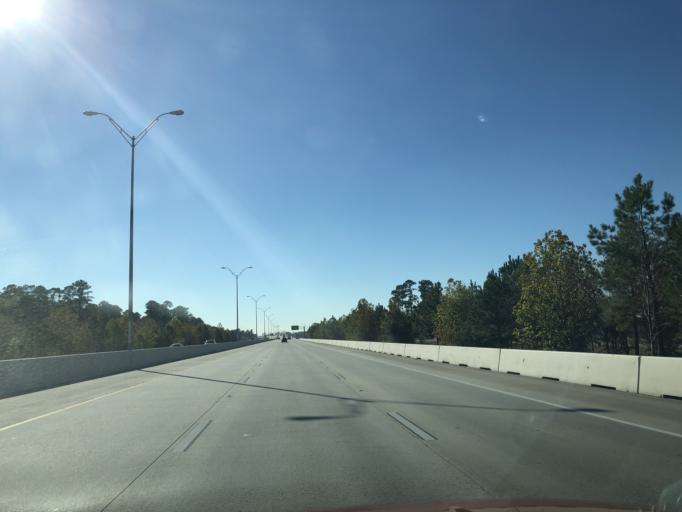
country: US
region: Texas
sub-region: Harris County
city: Sheldon
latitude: 29.8636
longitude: -95.1873
